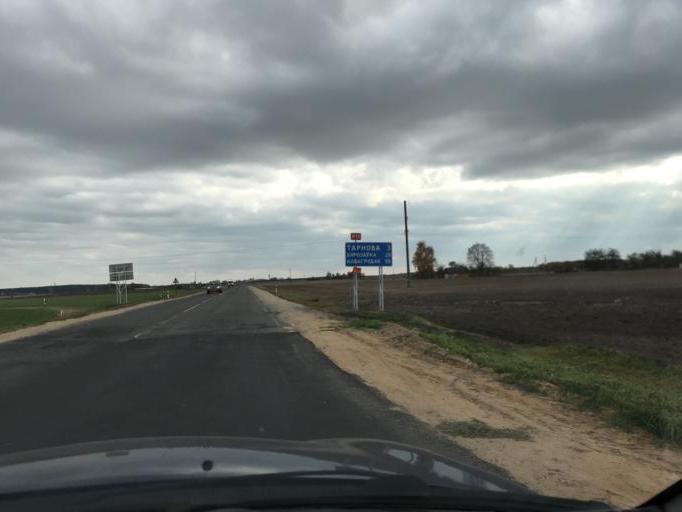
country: BY
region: Grodnenskaya
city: Lida
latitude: 53.8100
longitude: 25.1107
